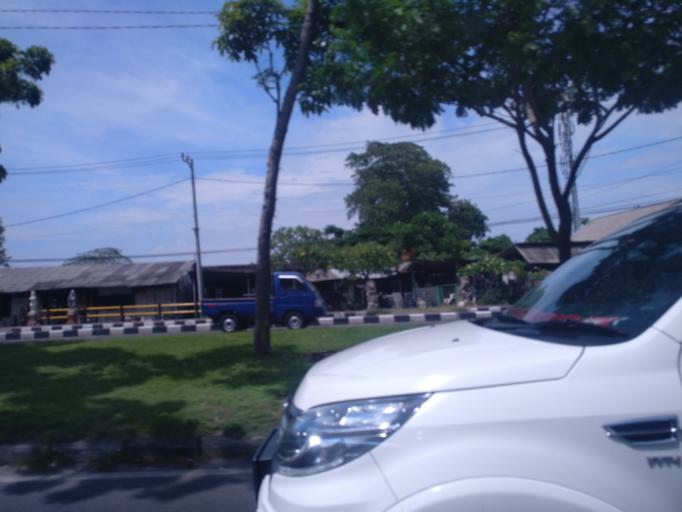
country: ID
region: Bali
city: Banjar Kertajiwa
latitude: -8.6495
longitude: 115.2617
